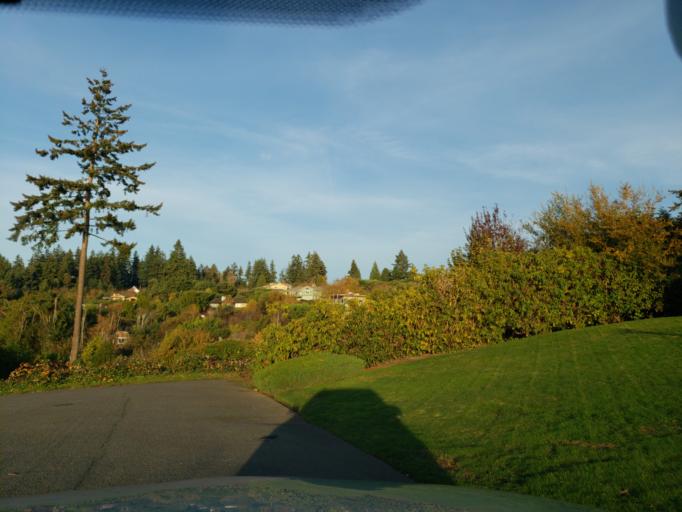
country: US
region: Washington
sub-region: King County
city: Shoreline
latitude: 47.7624
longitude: -122.3720
